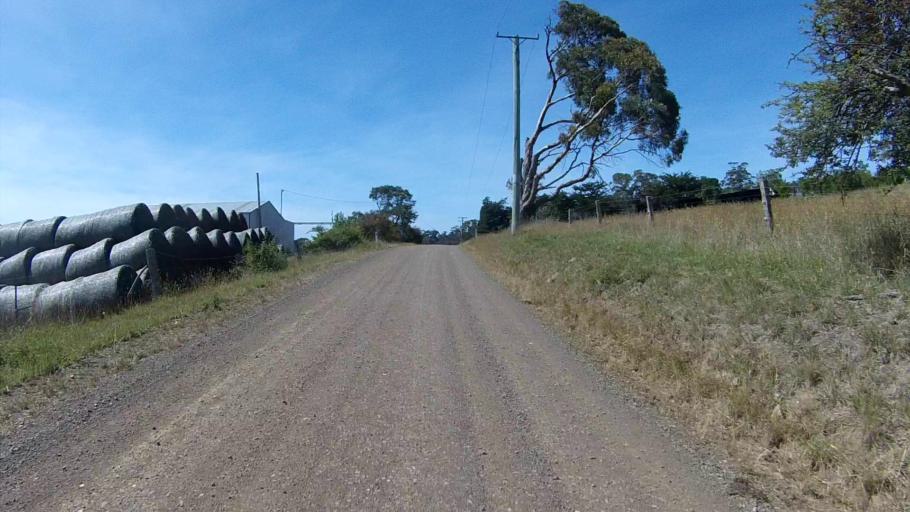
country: AU
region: Tasmania
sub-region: Sorell
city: Sorell
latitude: -42.7411
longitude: 147.5996
